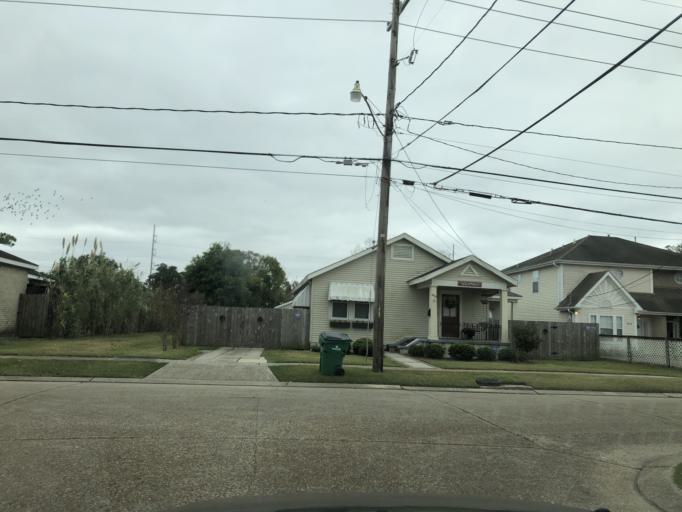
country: US
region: Louisiana
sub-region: Jefferson Parish
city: Metairie Terrace
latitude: 29.9784
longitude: -90.1630
